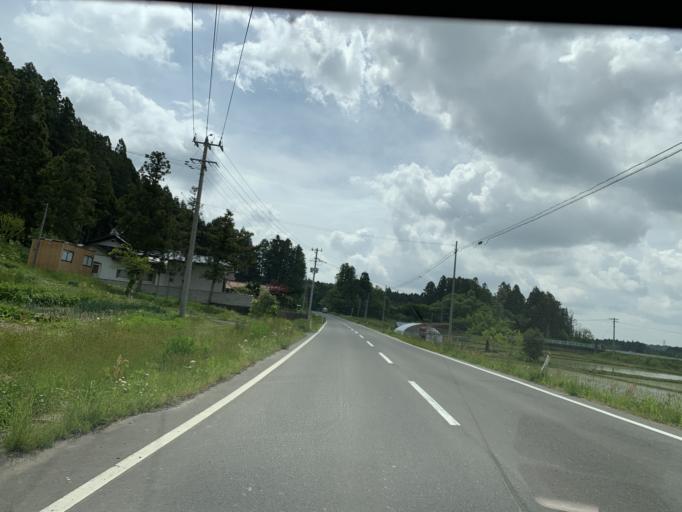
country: JP
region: Iwate
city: Ichinoseki
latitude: 38.8342
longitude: 141.0187
